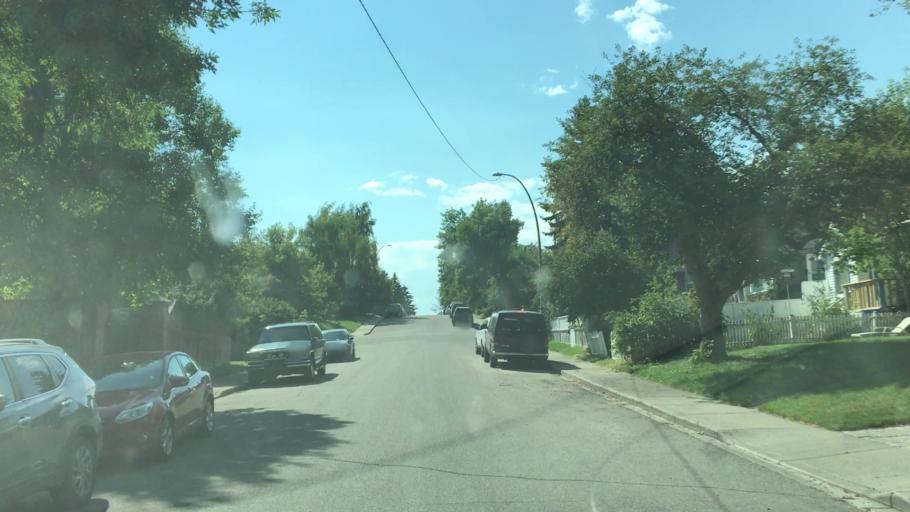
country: CA
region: Alberta
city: Calgary
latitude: 51.0796
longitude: -114.0641
